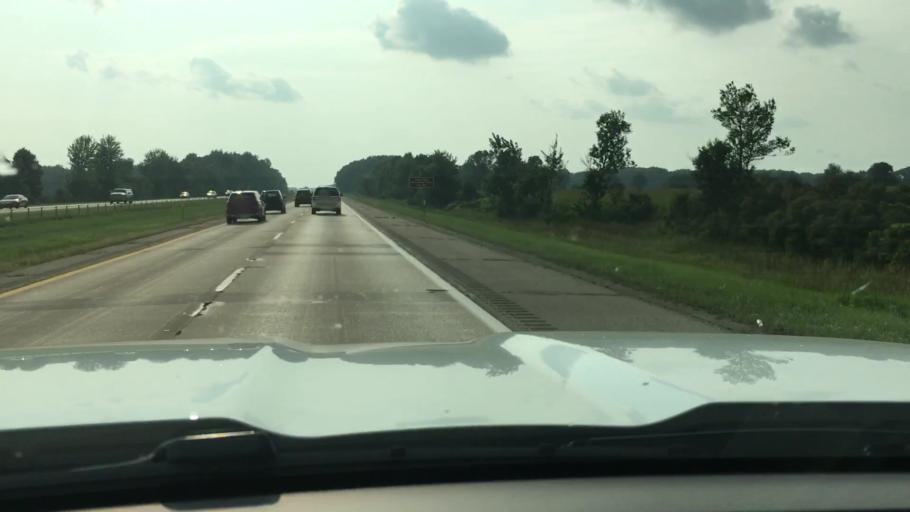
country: US
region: Michigan
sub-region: Ionia County
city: Lake Odessa
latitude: 42.8799
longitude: -85.1136
